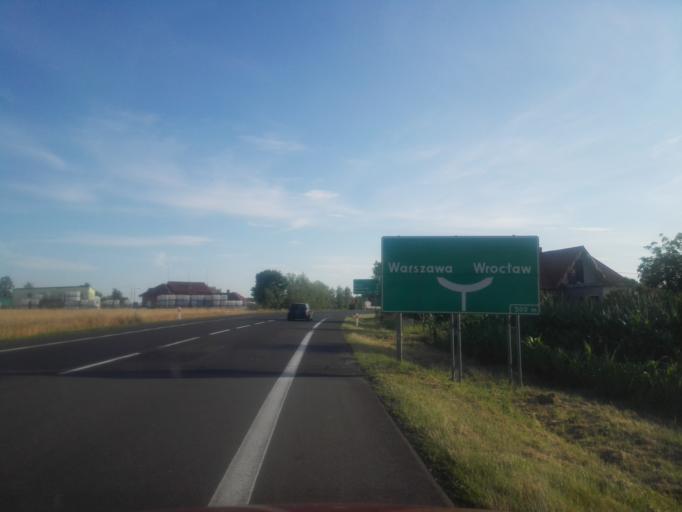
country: PL
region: Lodz Voivodeship
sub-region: Powiat wieruszowski
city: Walichnowy
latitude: 51.3099
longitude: 18.3822
